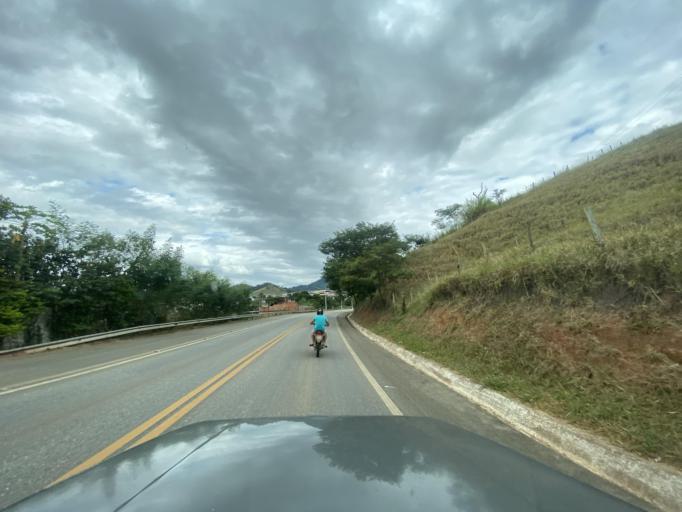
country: BR
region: Espirito Santo
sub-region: Alegre
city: Alegre
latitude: -20.7541
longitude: -41.4621
